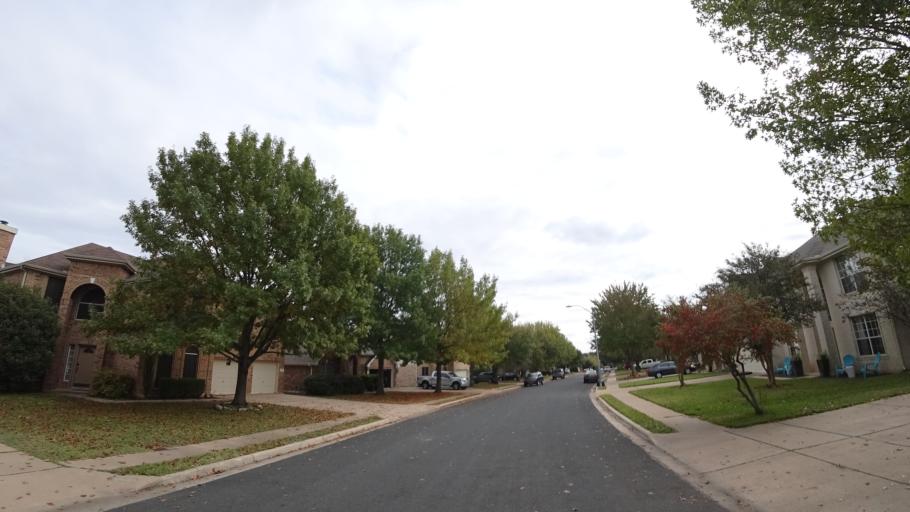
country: US
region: Texas
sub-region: Travis County
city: Wells Branch
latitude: 30.4437
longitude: -97.6744
